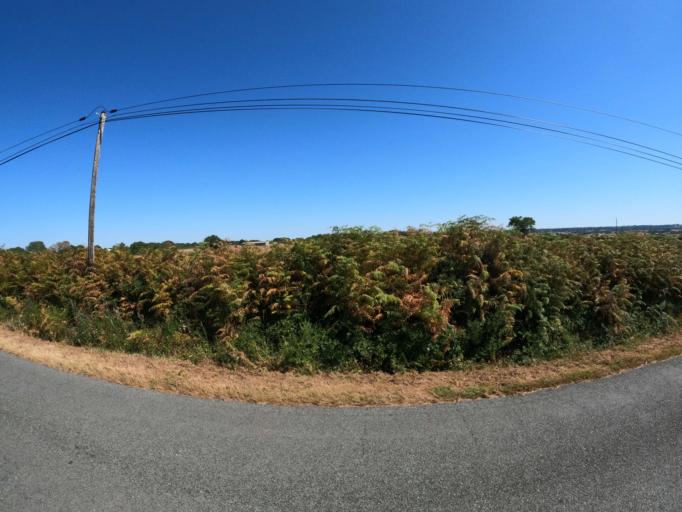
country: FR
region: Pays de la Loire
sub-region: Departement de la Vendee
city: Saint-Aubin-des-Ormeaux
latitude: 47.0110
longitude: -1.0003
